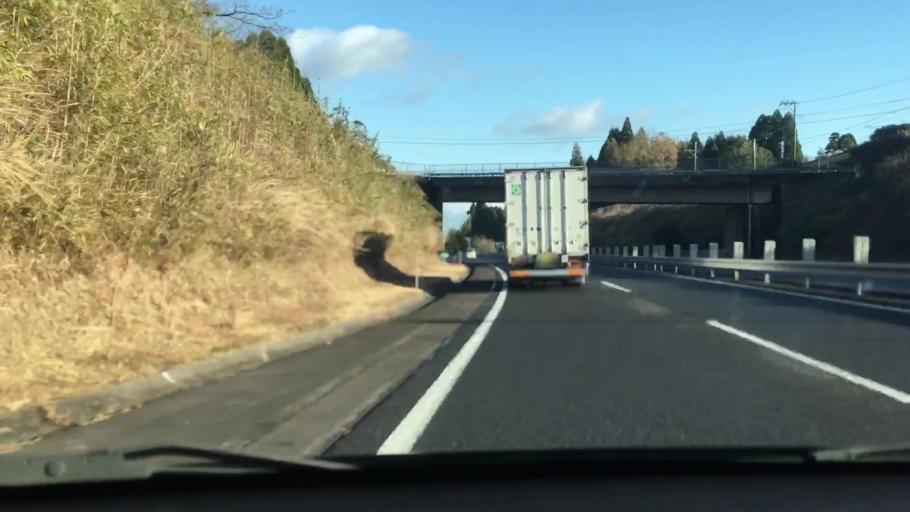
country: JP
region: Kagoshima
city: Kajiki
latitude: 31.8200
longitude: 130.6973
